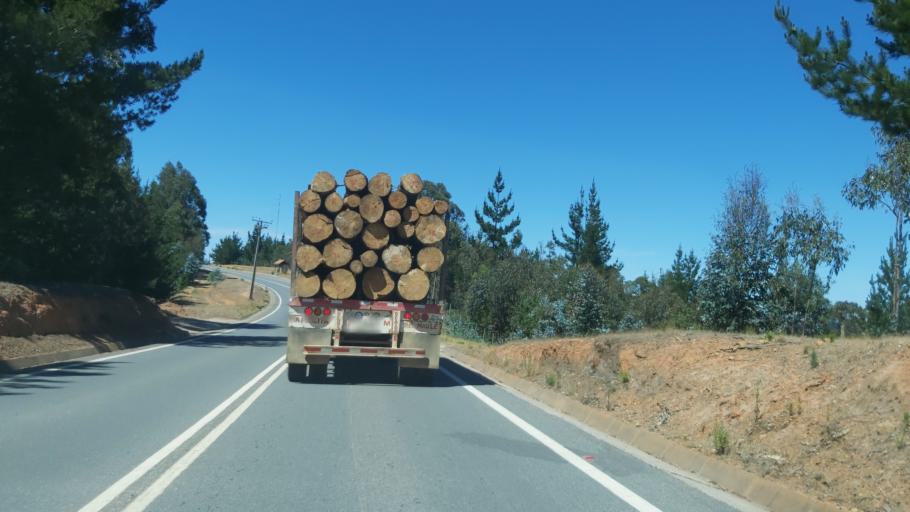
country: CL
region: Maule
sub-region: Provincia de Talca
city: Constitucion
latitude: -34.9273
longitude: -71.9871
